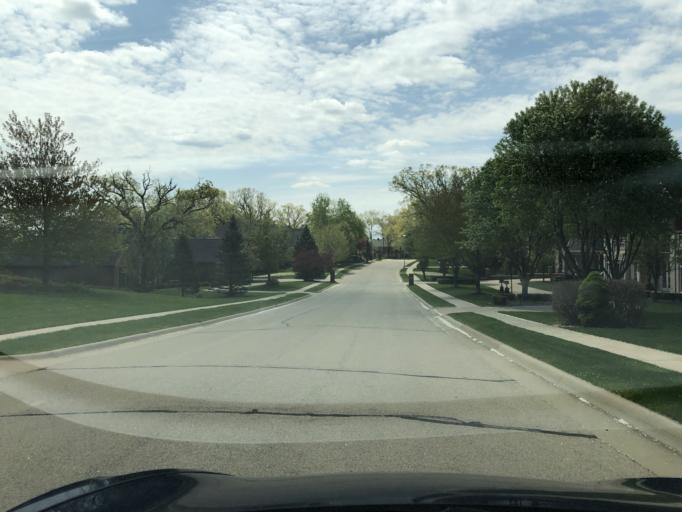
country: US
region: Iowa
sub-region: Dubuque County
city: Dubuque
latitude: 42.4749
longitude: -90.6623
